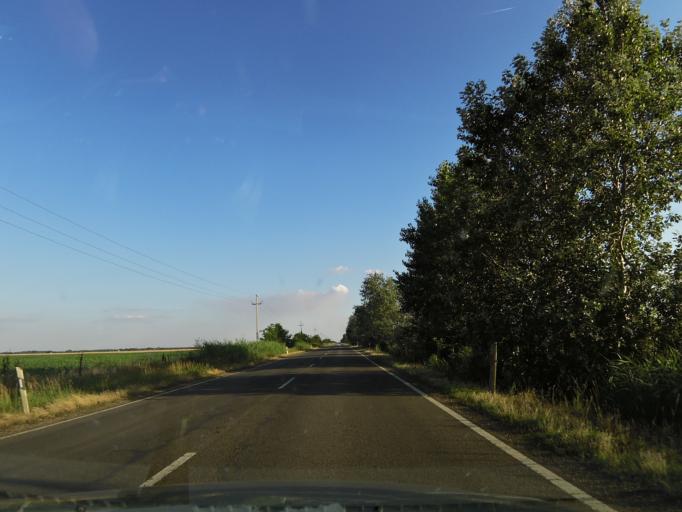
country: HU
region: Jasz-Nagykun-Szolnok
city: Tiszafoldvar
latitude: 46.9325
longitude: 20.2676
